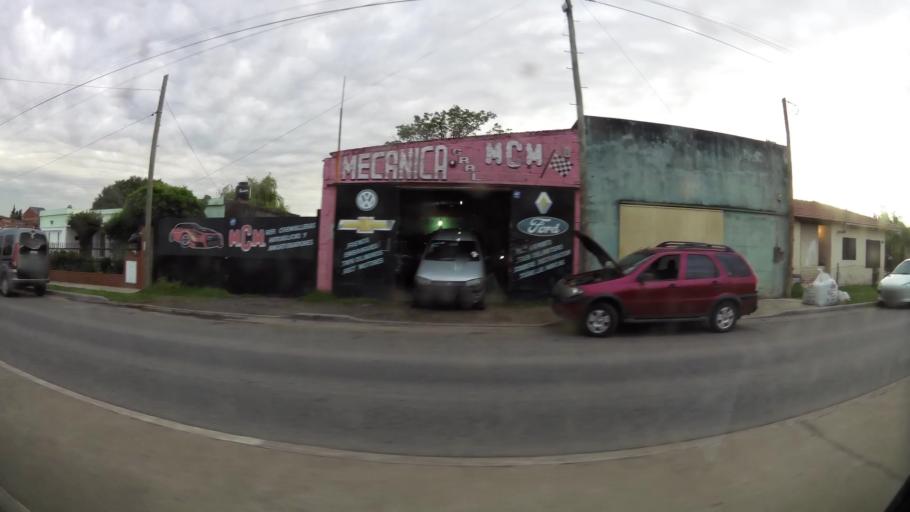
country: AR
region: Buenos Aires
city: San Nicolas de los Arroyos
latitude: -33.3572
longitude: -60.2003
